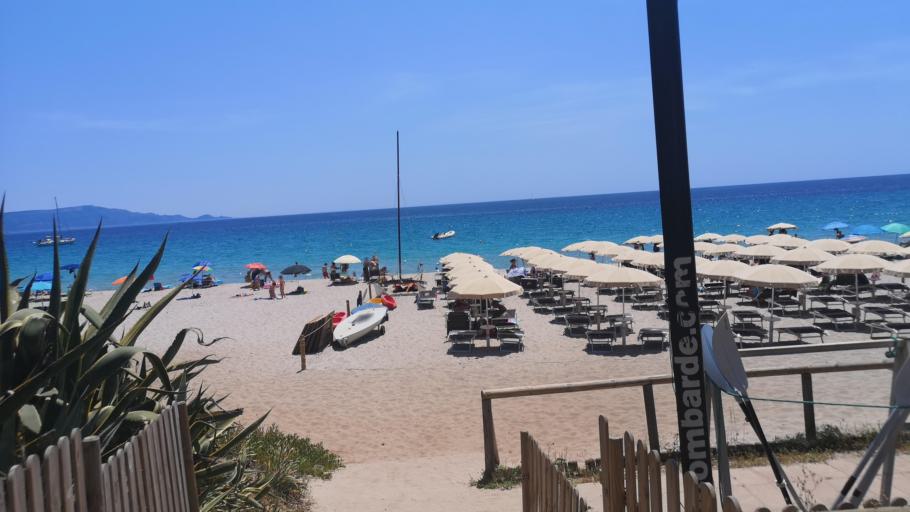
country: IT
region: Sardinia
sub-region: Provincia di Sassari
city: Alghero
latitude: 40.5845
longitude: 8.2582
